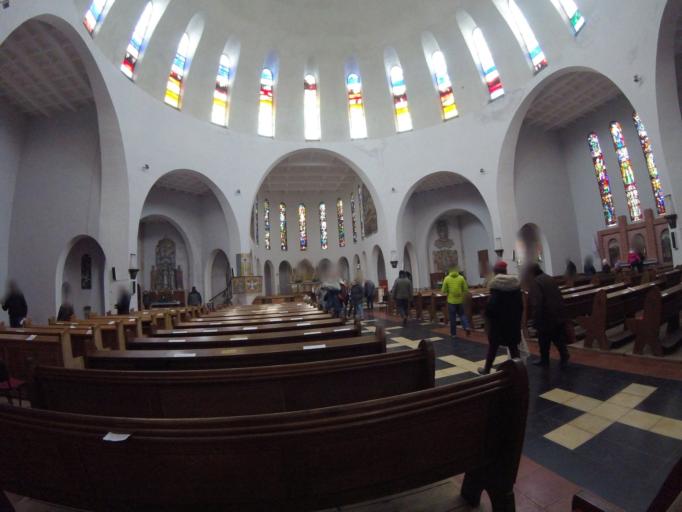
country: HU
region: Baranya
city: Mohacs
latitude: 45.9900
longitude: 18.6894
